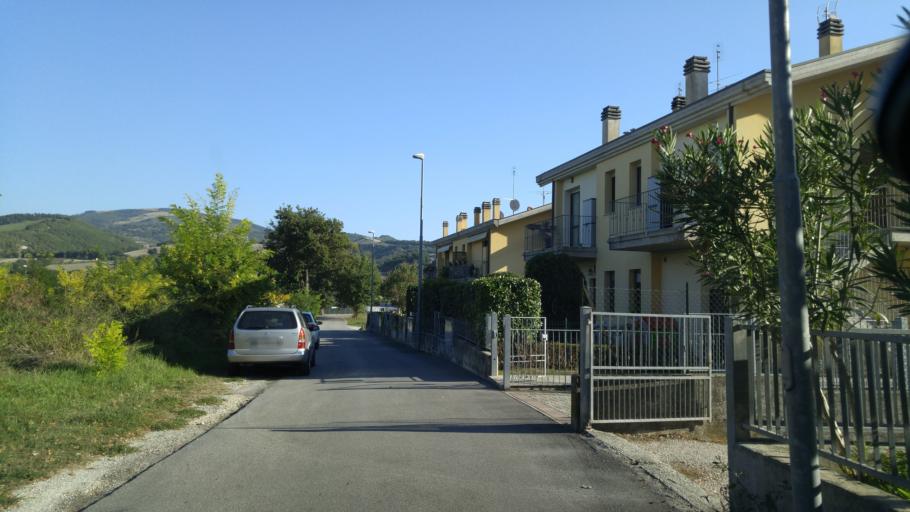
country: IT
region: The Marches
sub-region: Provincia di Pesaro e Urbino
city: Fermignano
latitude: 43.6905
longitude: 12.6453
